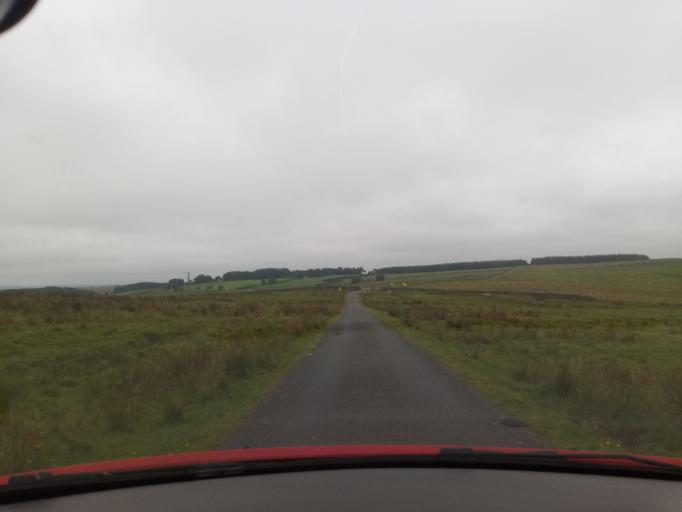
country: GB
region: England
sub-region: Northumberland
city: Otterburn
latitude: 55.2546
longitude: -2.1068
